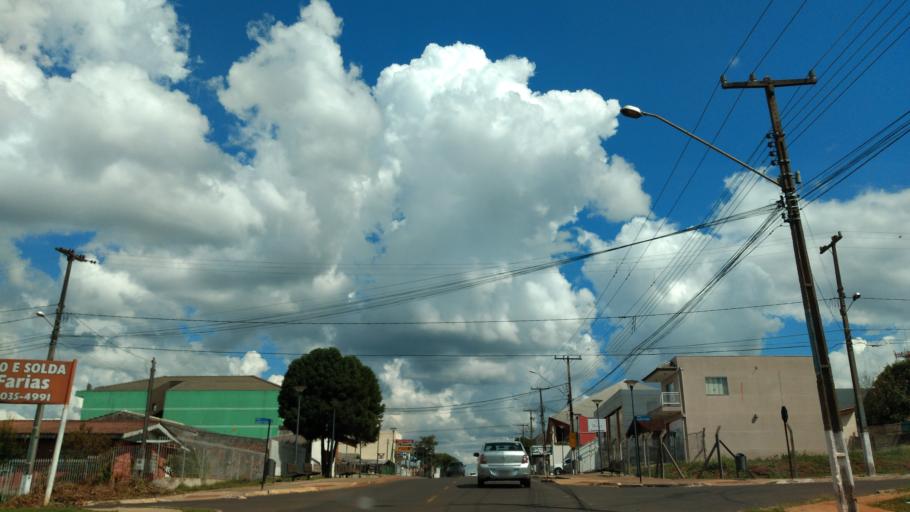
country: BR
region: Parana
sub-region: Guarapuava
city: Guarapuava
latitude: -25.3993
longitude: -51.4935
